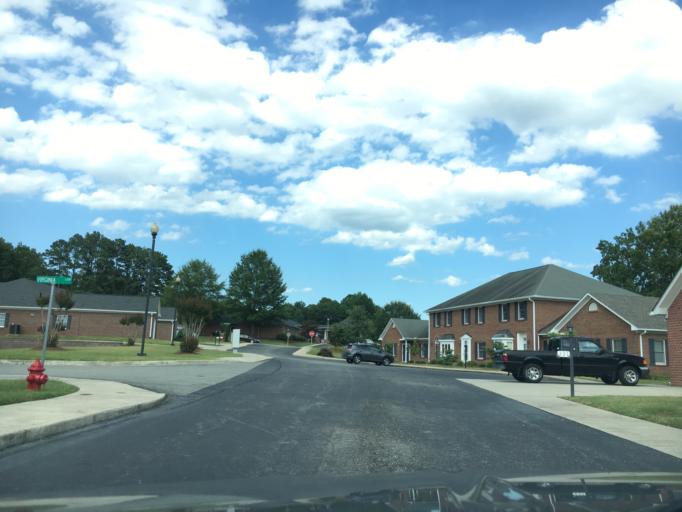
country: US
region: Virginia
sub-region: Halifax County
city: South Boston
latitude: 36.7139
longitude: -78.9184
